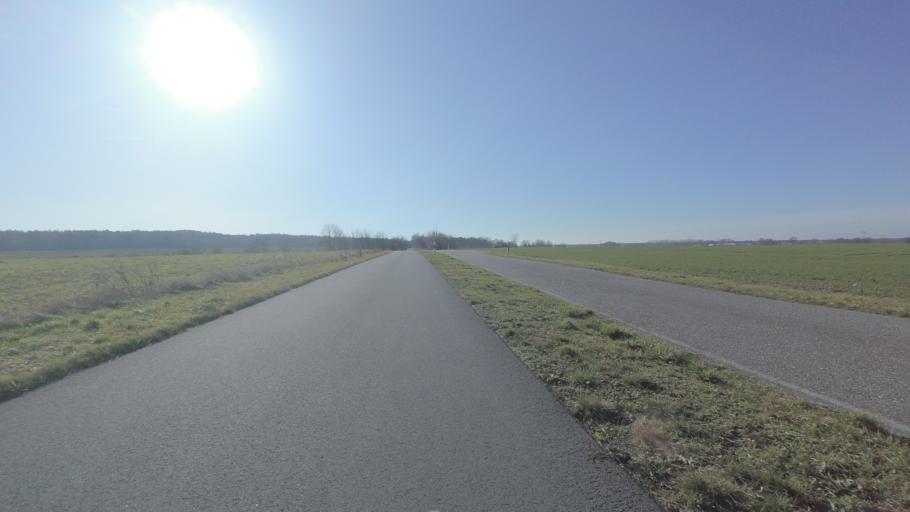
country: DE
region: Brandenburg
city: Luckenwalde
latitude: 52.0374
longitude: 13.1351
